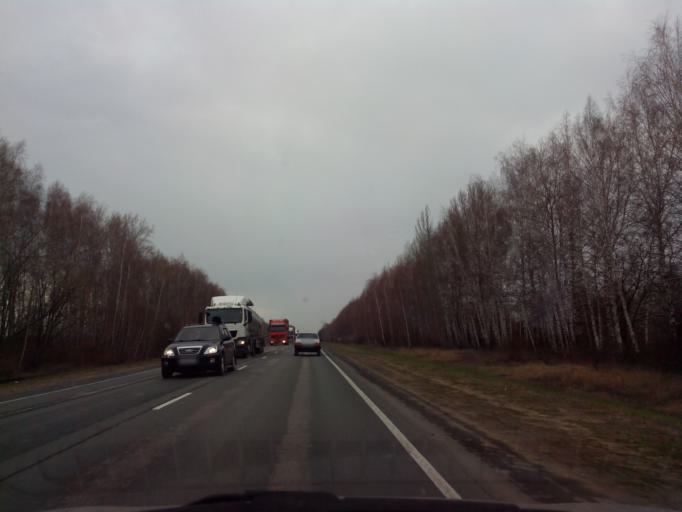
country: RU
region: Tambov
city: Michurinsk
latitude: 53.0674
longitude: 40.4375
